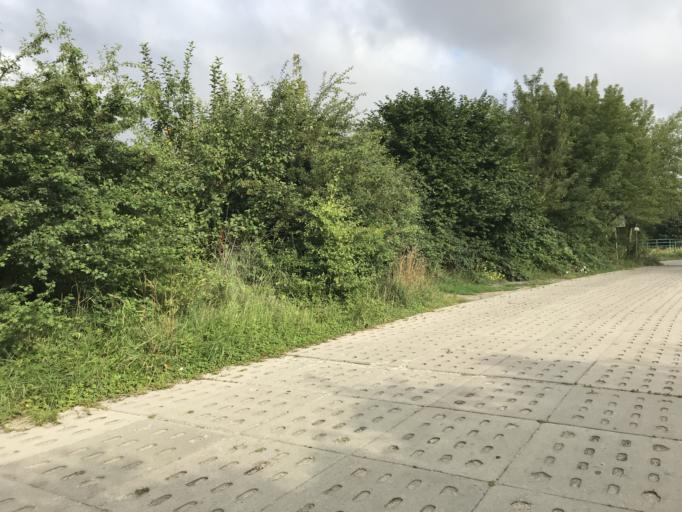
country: PL
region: Pomeranian Voivodeship
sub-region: Gdansk
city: Gdansk
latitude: 54.3445
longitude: 18.6739
